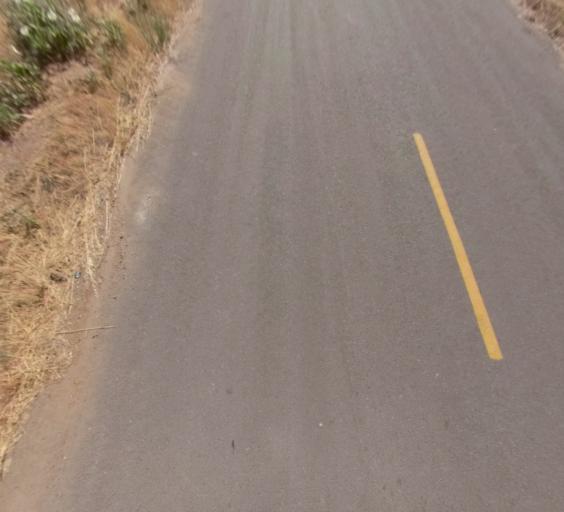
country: US
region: California
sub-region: Madera County
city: Parksdale
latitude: 36.9853
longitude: -120.0173
